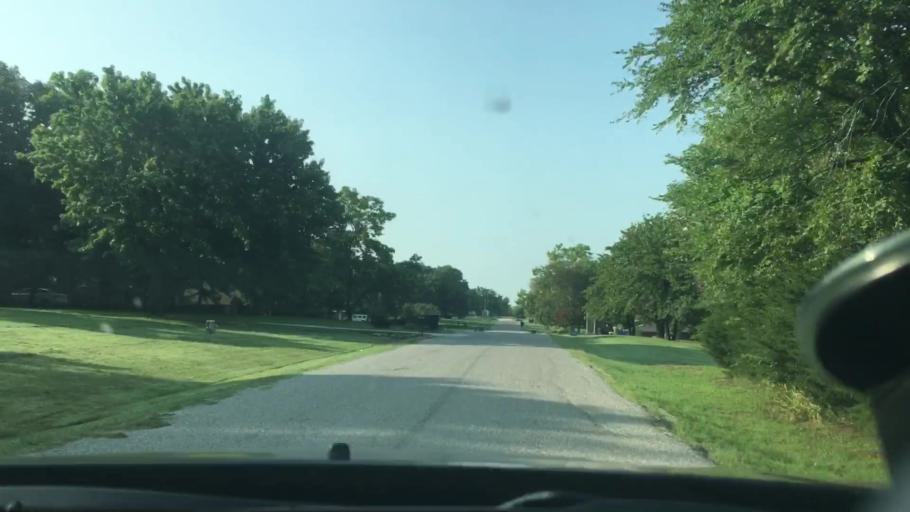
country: US
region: Oklahoma
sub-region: Pontotoc County
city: Ada
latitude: 34.7871
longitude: -96.7397
